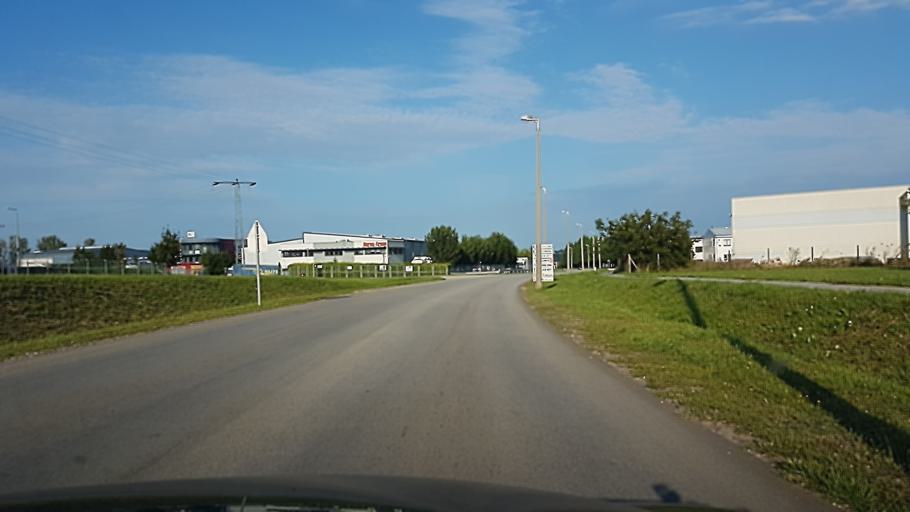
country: HU
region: Fejer
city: Pakozd
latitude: 47.1826
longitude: 18.4780
